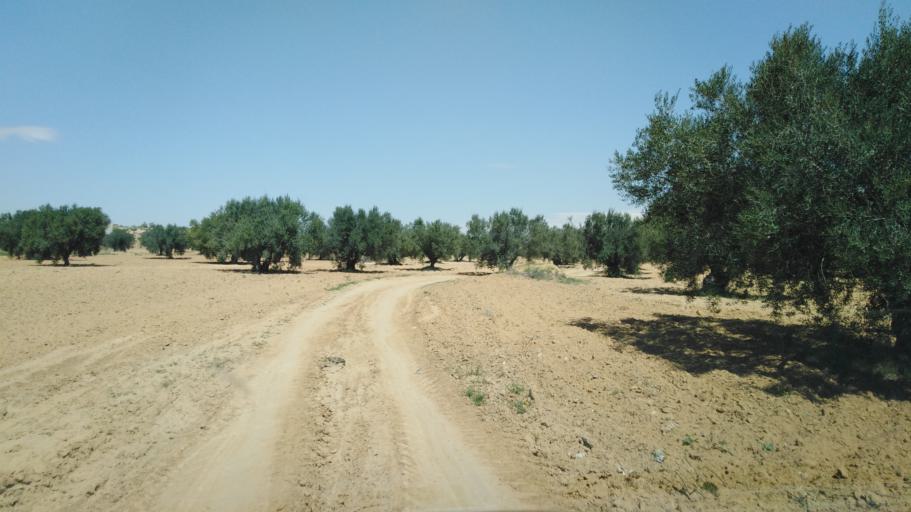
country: TN
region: Safaqis
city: Sfax
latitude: 34.7825
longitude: 10.5279
